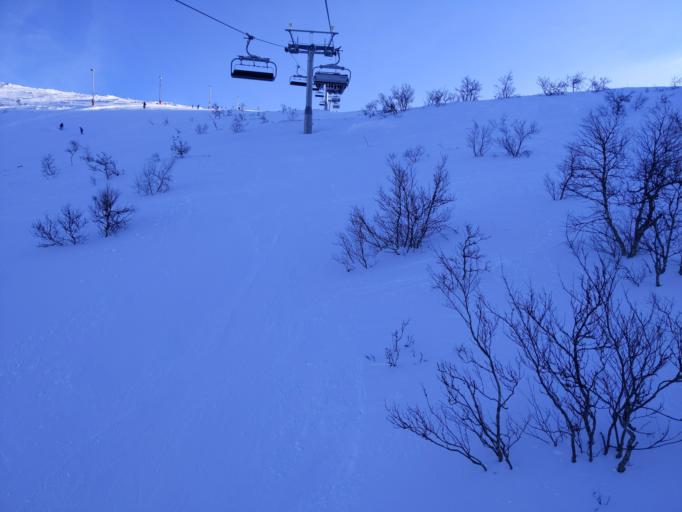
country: SE
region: Jaemtland
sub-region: Harjedalens Kommun
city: Sveg
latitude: 62.4141
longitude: 13.9837
